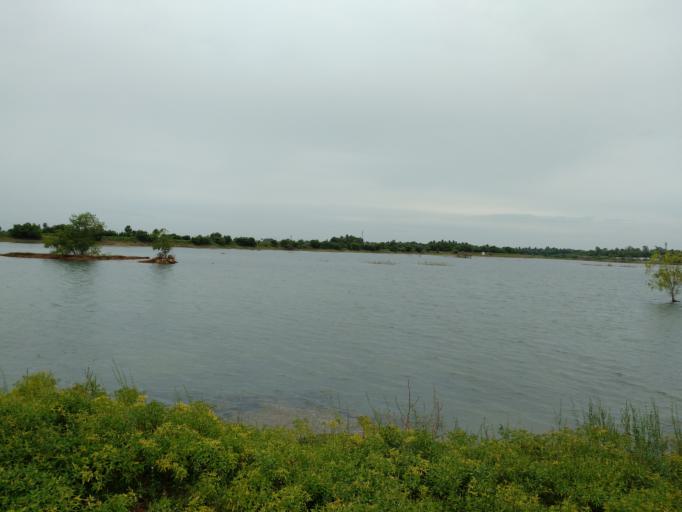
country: IN
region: Tamil Nadu
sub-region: Kancheepuram
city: Nandambakkam
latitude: 12.9518
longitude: 80.0562
